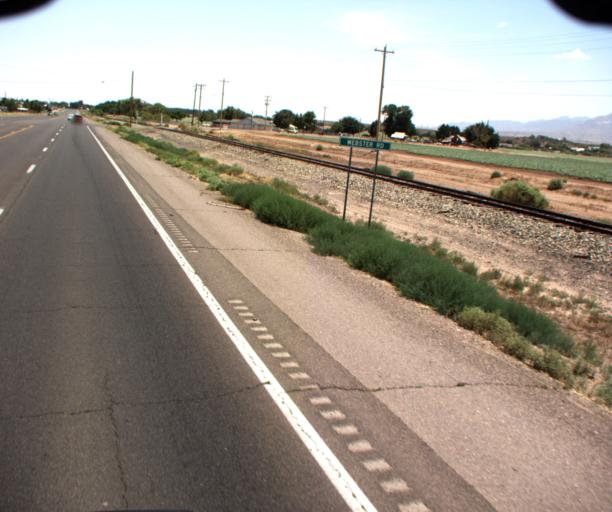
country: US
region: Arizona
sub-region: Graham County
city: Thatcher
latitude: 32.8598
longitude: -109.7851
